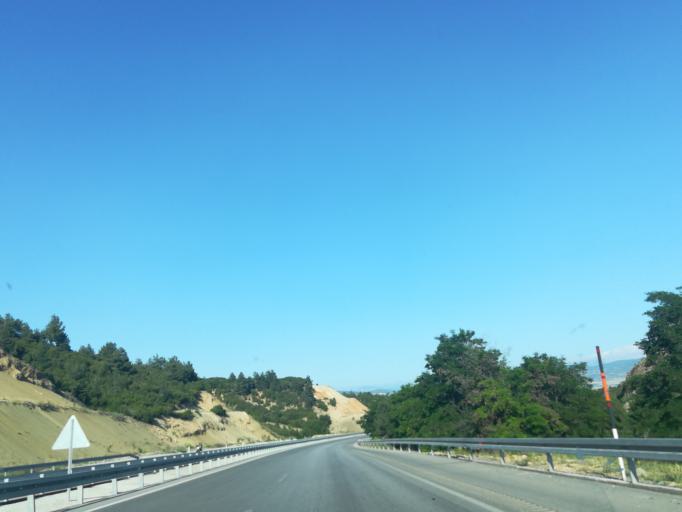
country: TR
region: Isparta
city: Keciborlu
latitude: 37.9174
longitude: 30.2754
